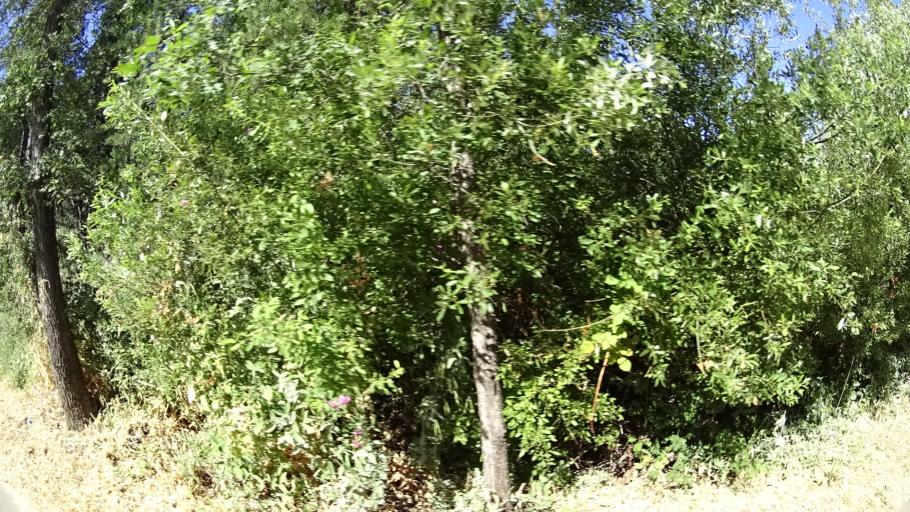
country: US
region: California
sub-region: Amador County
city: Pioneer
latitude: 38.3999
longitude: -120.5177
